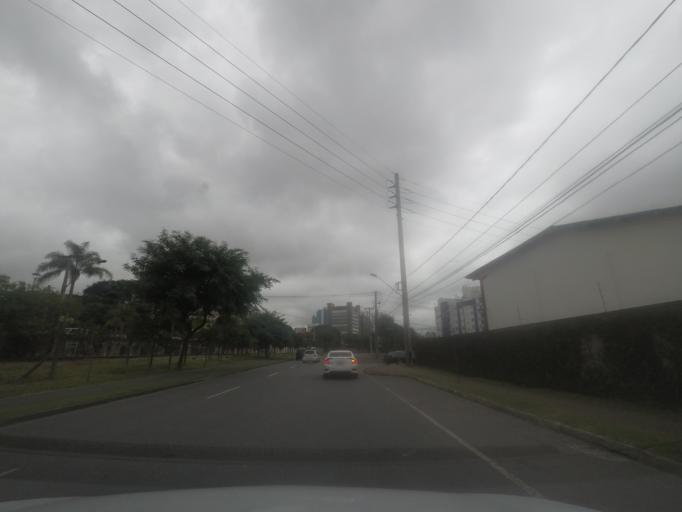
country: BR
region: Parana
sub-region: Curitiba
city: Curitiba
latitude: -25.4360
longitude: -49.2503
